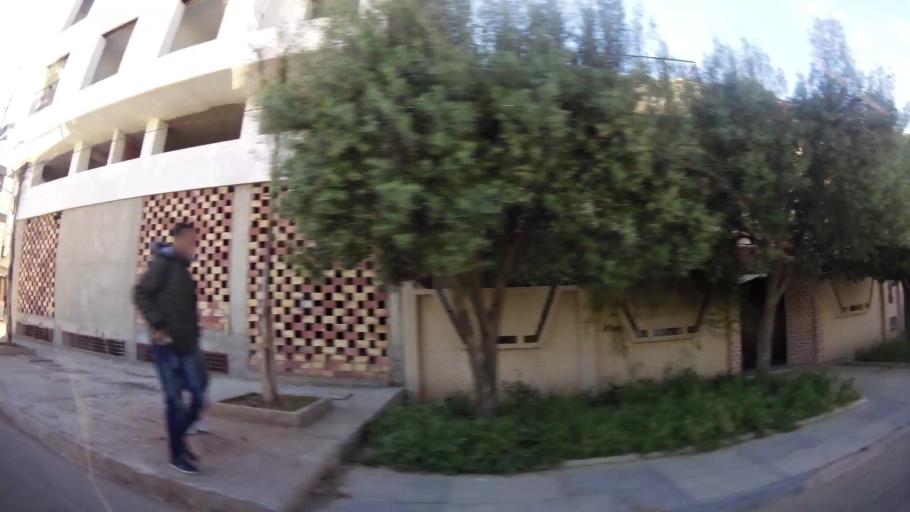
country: MA
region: Oriental
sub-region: Oujda-Angad
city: Oujda
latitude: 34.6538
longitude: -1.8946
